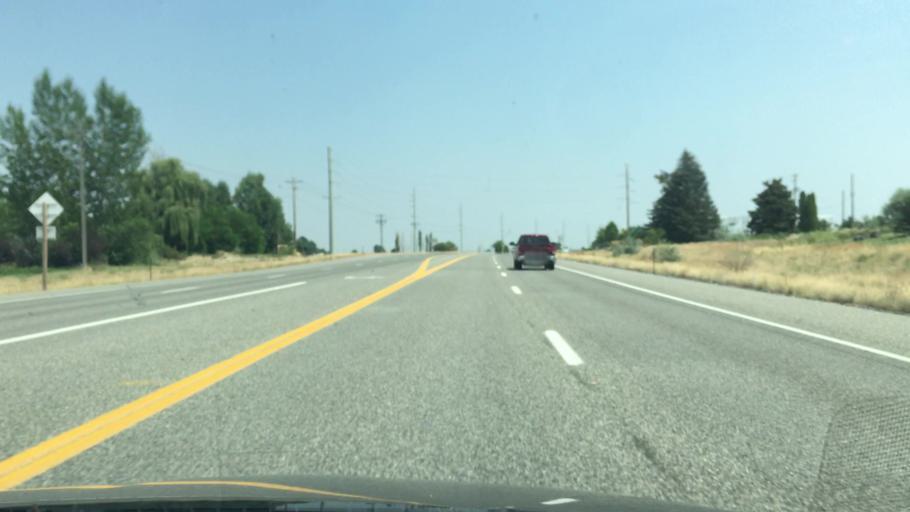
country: US
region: Idaho
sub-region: Twin Falls County
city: Twin Falls
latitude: 42.5936
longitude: -114.5236
